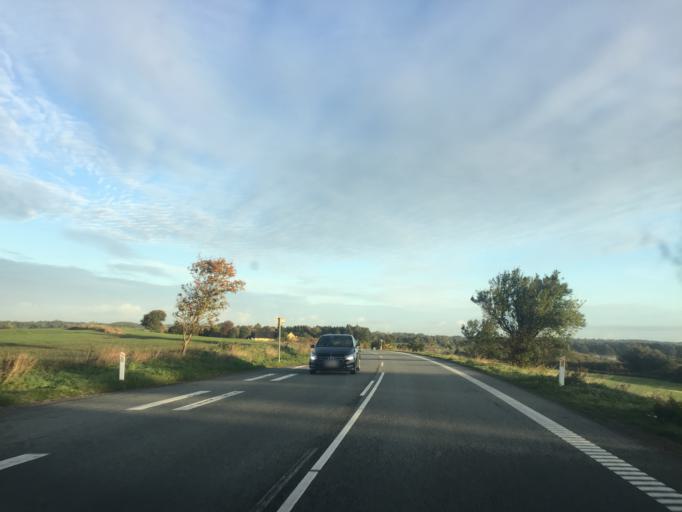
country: DK
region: Capital Region
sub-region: Egedal Kommune
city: Smorumnedre
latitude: 55.7667
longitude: 12.2944
